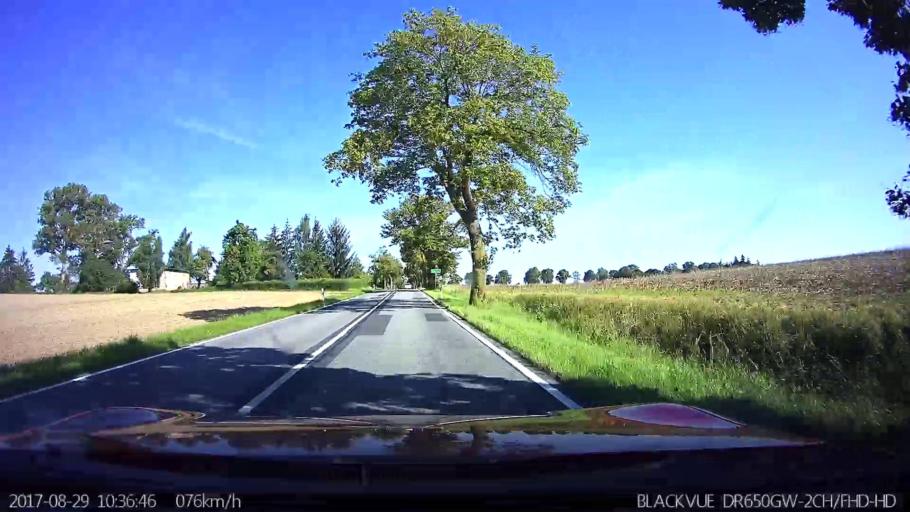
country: DE
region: Mecklenburg-Vorpommern
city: Tribsees
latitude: 54.1495
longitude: 12.8033
